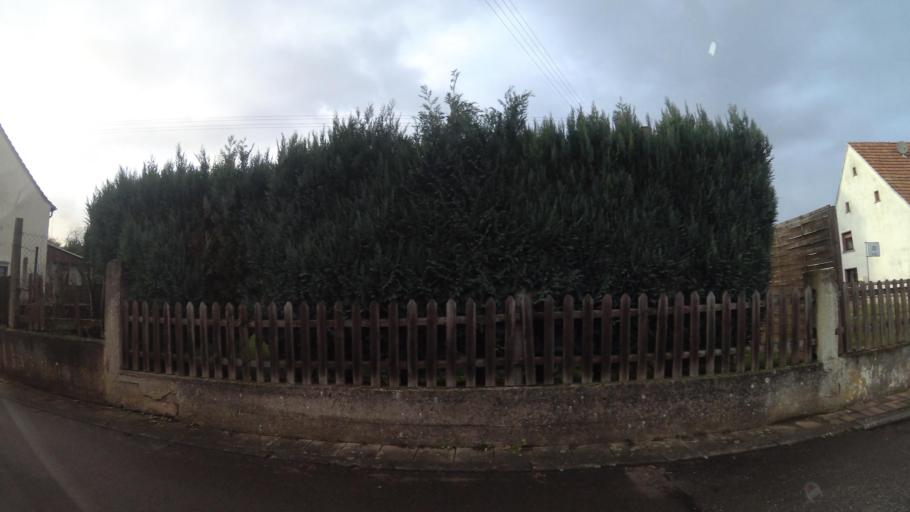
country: DE
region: Rheinland-Pfalz
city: Ulmet
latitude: 49.5844
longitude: 7.4548
